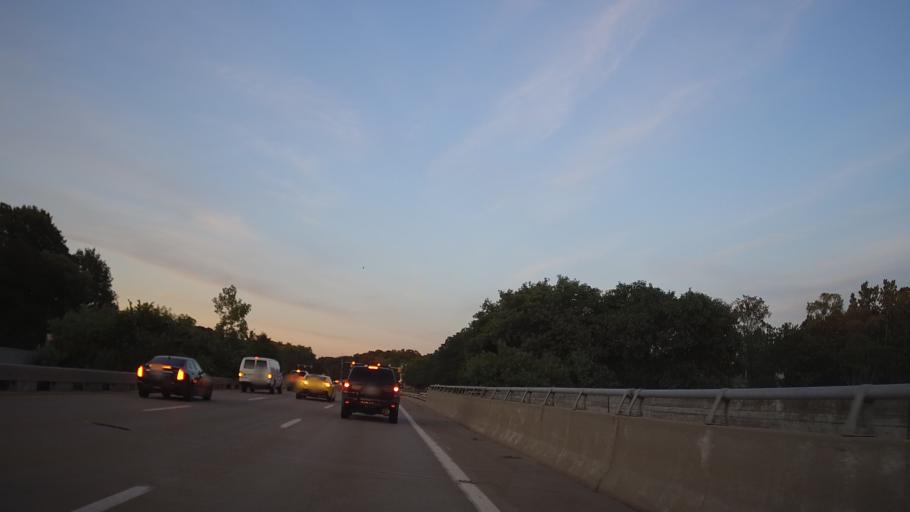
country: US
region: Michigan
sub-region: Macomb County
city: Fraser
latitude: 42.5664
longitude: -82.9715
